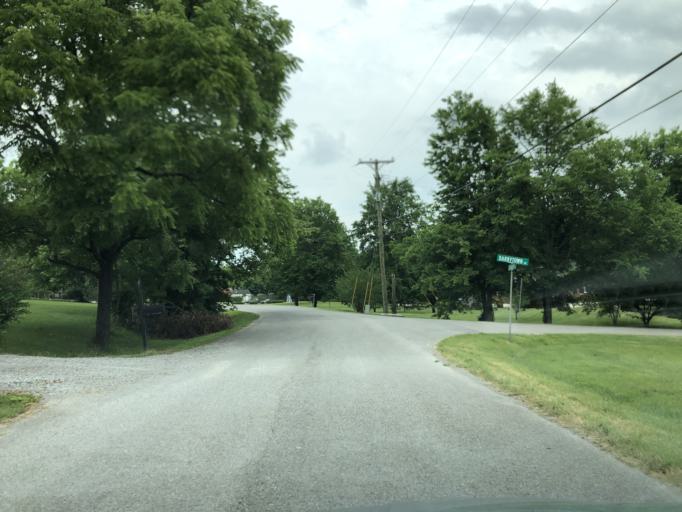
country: US
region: Tennessee
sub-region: Davidson County
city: Goodlettsville
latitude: 36.2665
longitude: -86.7646
